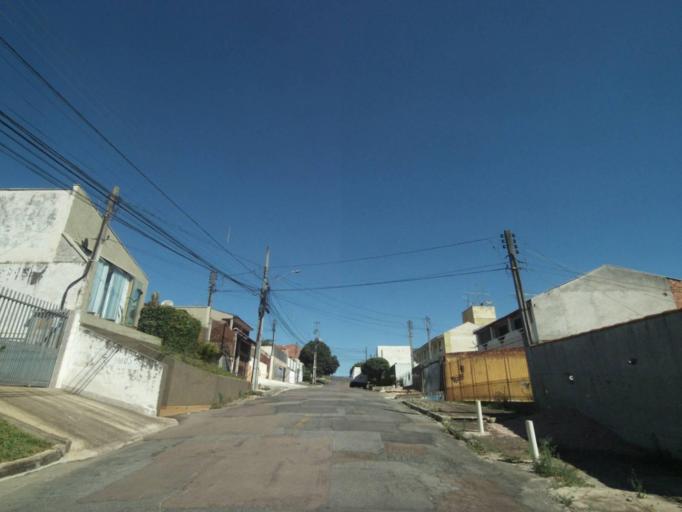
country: BR
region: Parana
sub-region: Curitiba
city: Curitiba
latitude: -25.4588
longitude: -49.3524
